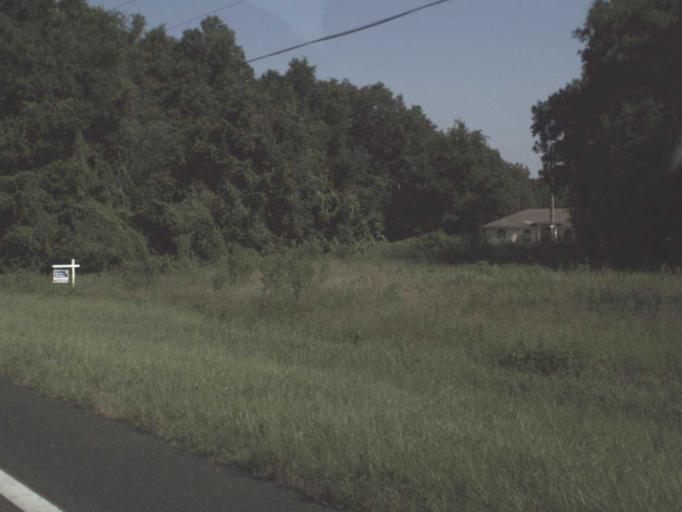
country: US
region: Florida
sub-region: Polk County
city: Willow Oak
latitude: 27.9299
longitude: -82.0782
